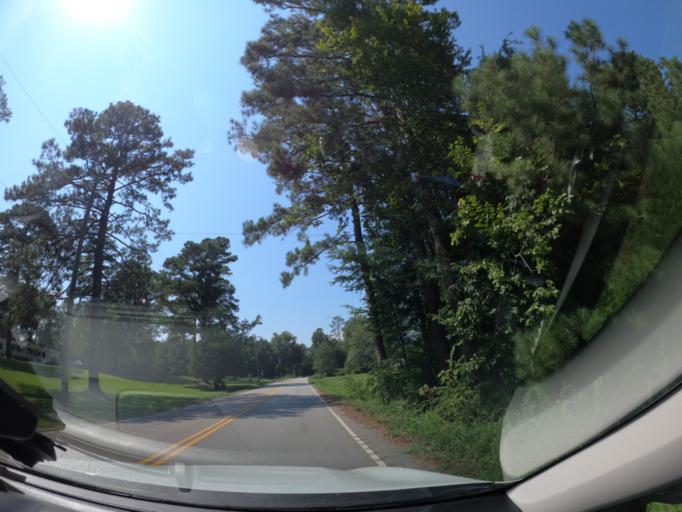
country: US
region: South Carolina
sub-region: Richland County
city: Hopkins
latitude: 33.8498
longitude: -80.8729
